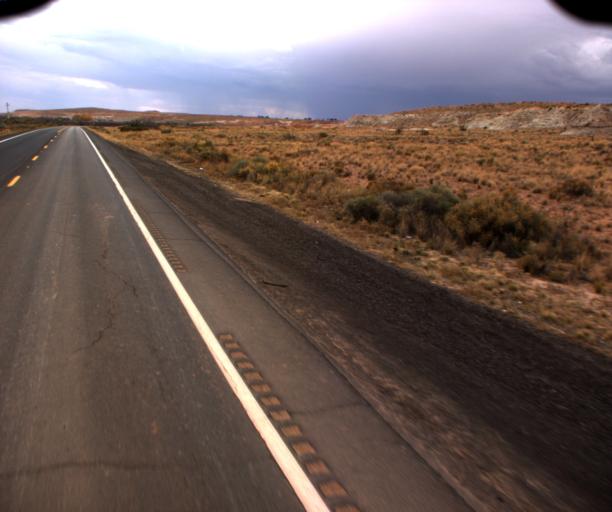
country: US
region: Arizona
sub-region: Coconino County
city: Kaibito
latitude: 36.3310
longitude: -110.9246
